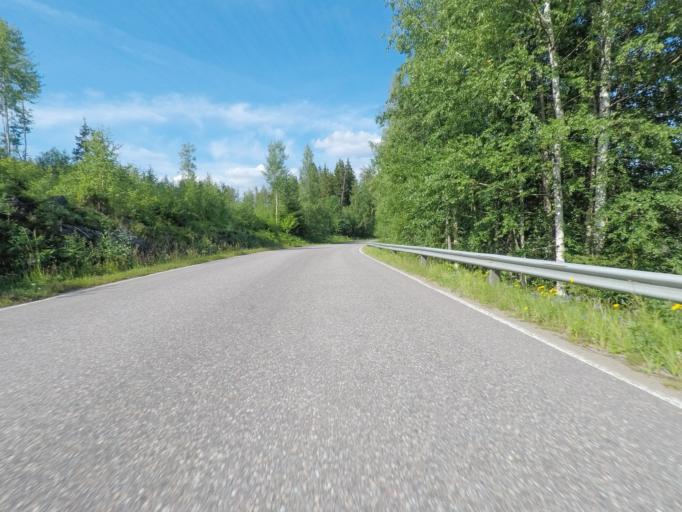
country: FI
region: Southern Savonia
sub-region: Mikkeli
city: Puumala
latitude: 61.6072
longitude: 28.2174
